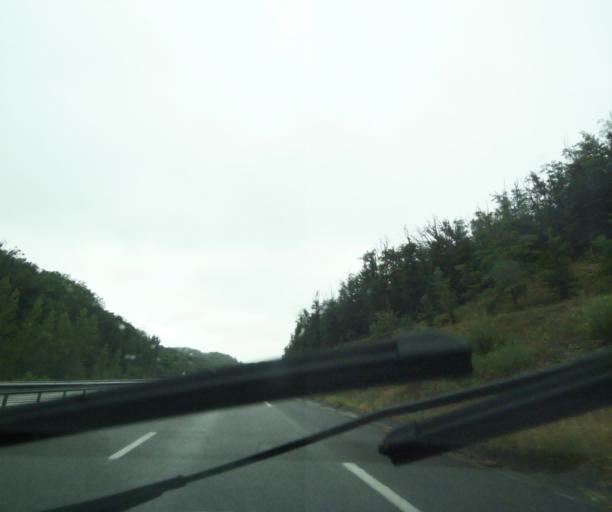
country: FR
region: Midi-Pyrenees
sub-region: Departement du Tarn
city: Le Garric
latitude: 43.9972
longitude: 2.1716
